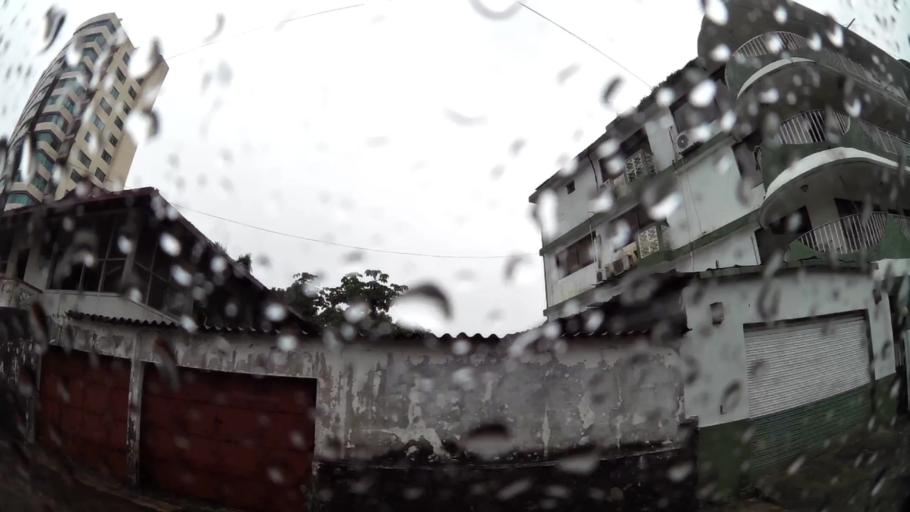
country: PA
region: Colon
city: Colon
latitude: 9.3637
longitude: -79.9075
